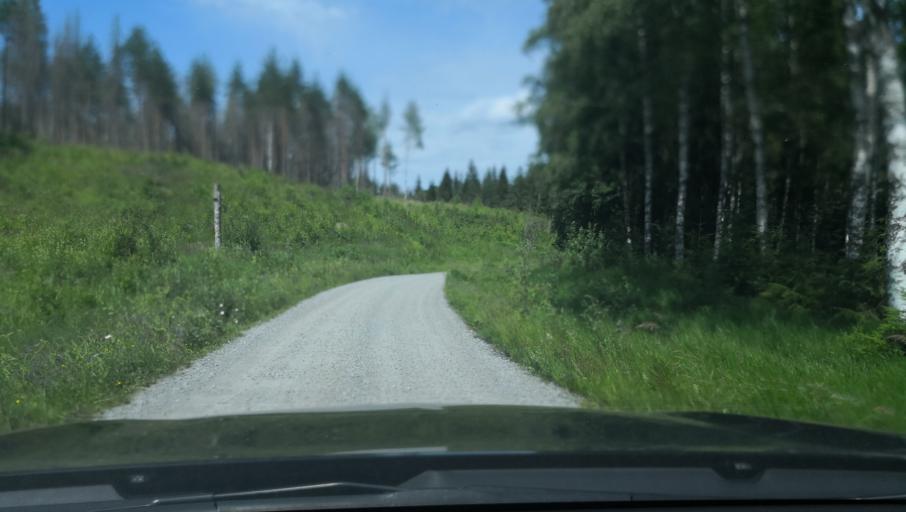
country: SE
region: Vaestmanland
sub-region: Surahammars Kommun
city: Ramnas
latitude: 59.8899
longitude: 16.0992
